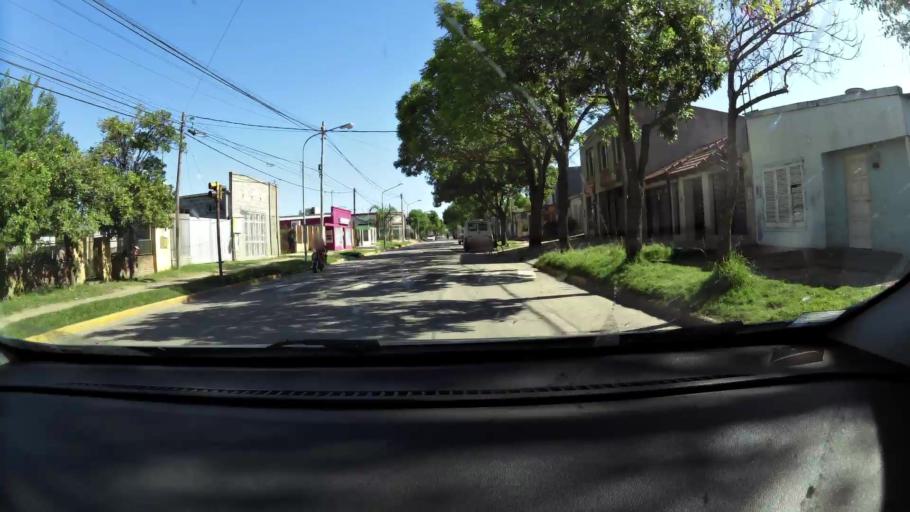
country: AR
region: Santa Fe
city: Rafaela
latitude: -31.2395
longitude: -61.4745
